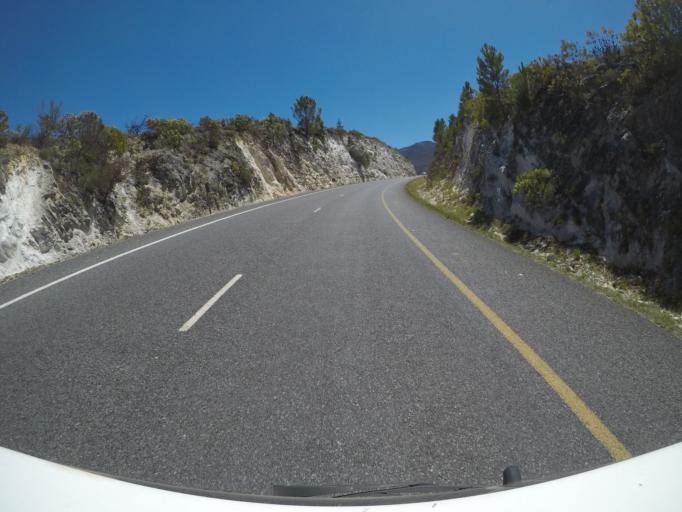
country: ZA
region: Western Cape
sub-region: Overberg District Municipality
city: Grabouw
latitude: -34.2203
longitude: 19.1741
